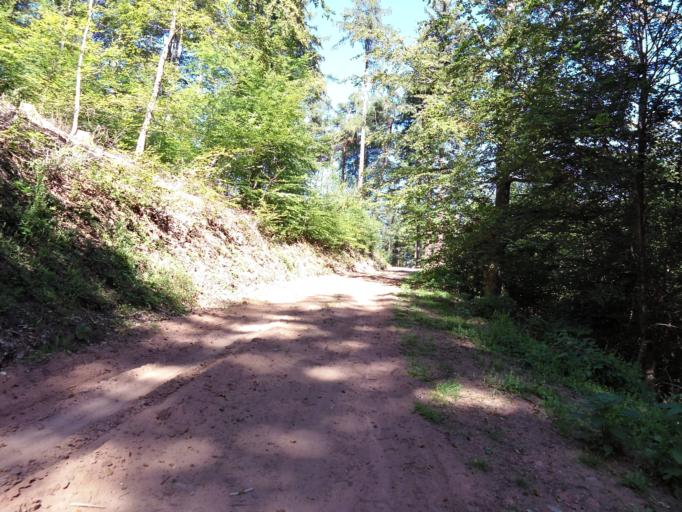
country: DE
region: Rheinland-Pfalz
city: Weidenthal
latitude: 49.3990
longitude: 7.9945
